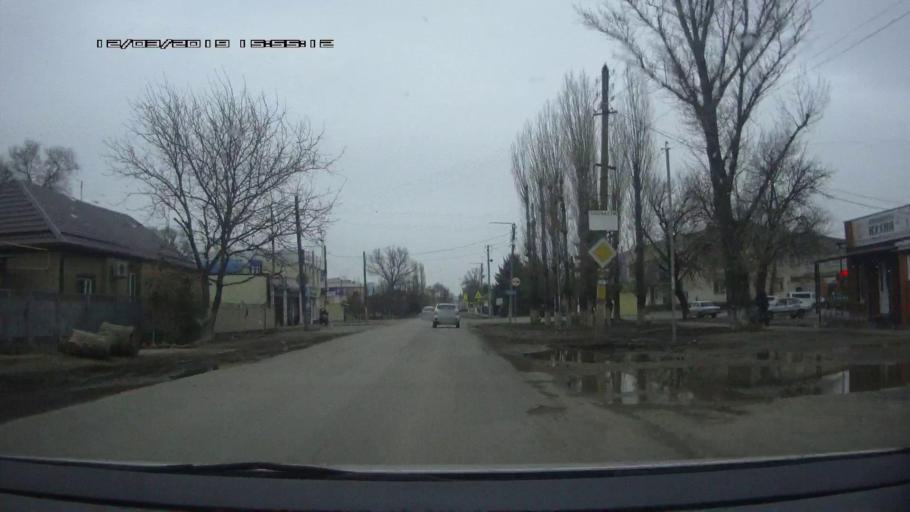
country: RU
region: Rostov
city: Novobataysk
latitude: 46.8953
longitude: 39.7793
